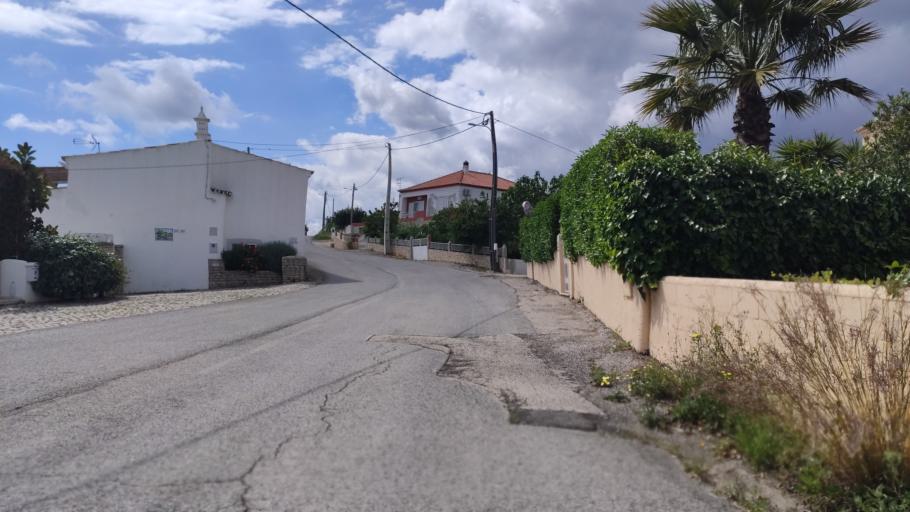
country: PT
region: Faro
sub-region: Sao Bras de Alportel
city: Sao Bras de Alportel
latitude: 37.1595
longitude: -7.9416
